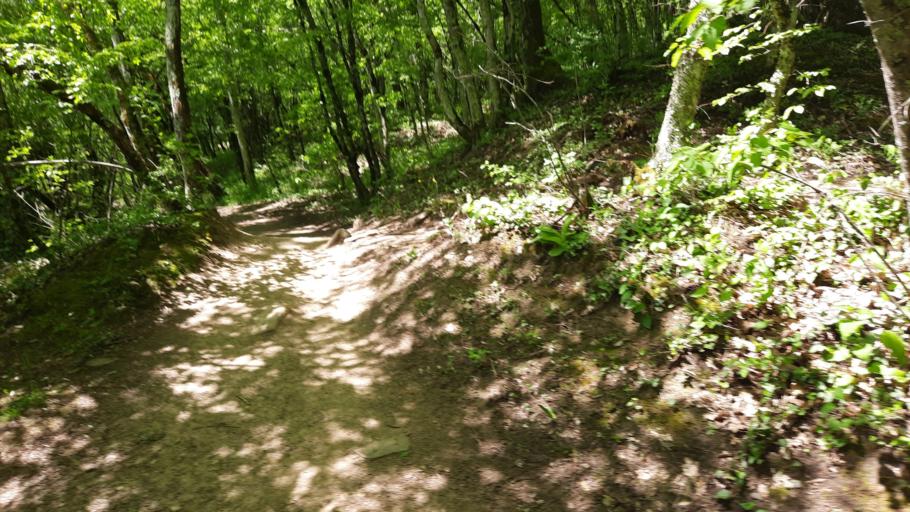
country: RU
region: Krasnodarskiy
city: Divnomorskoye
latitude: 44.5551
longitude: 38.2515
